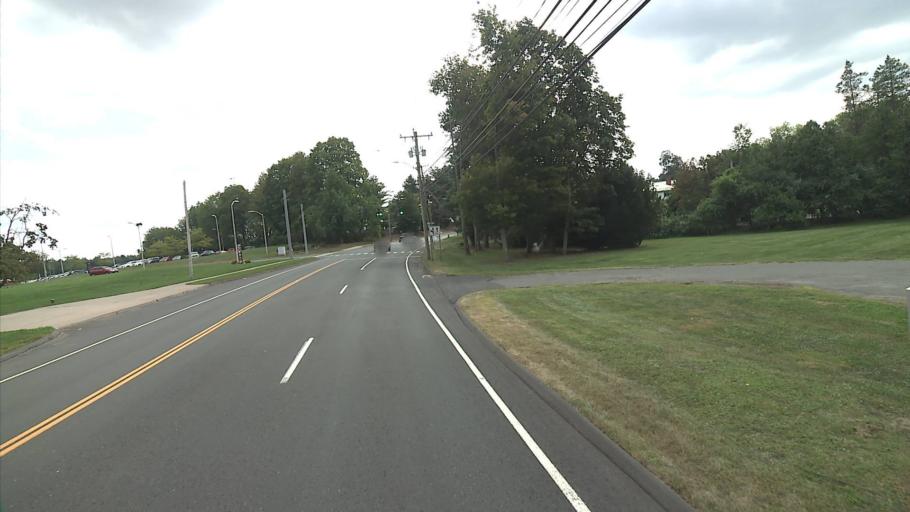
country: US
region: Connecticut
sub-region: Hartford County
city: Blue Hills
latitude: 41.7944
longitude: -72.7173
